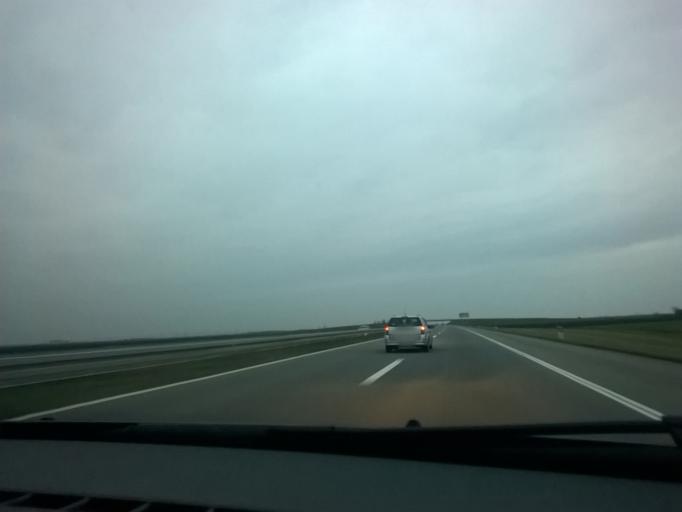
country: RS
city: Krcedin
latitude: 45.1070
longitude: 20.1065
